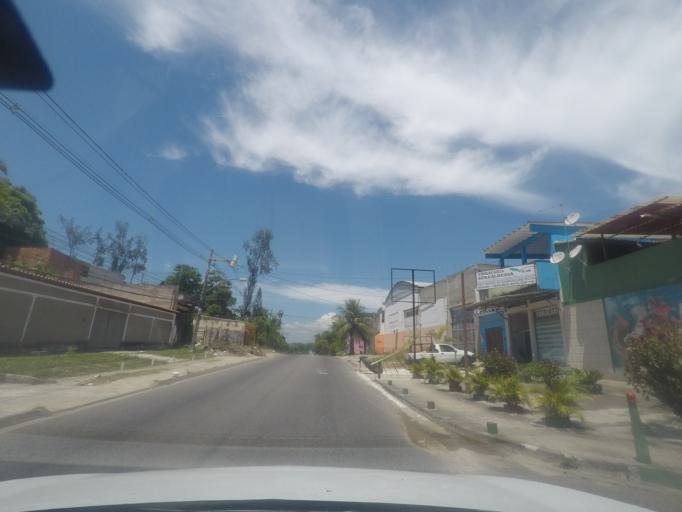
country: BR
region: Rio de Janeiro
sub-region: Itaguai
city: Itaguai
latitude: -22.9813
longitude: -43.6844
